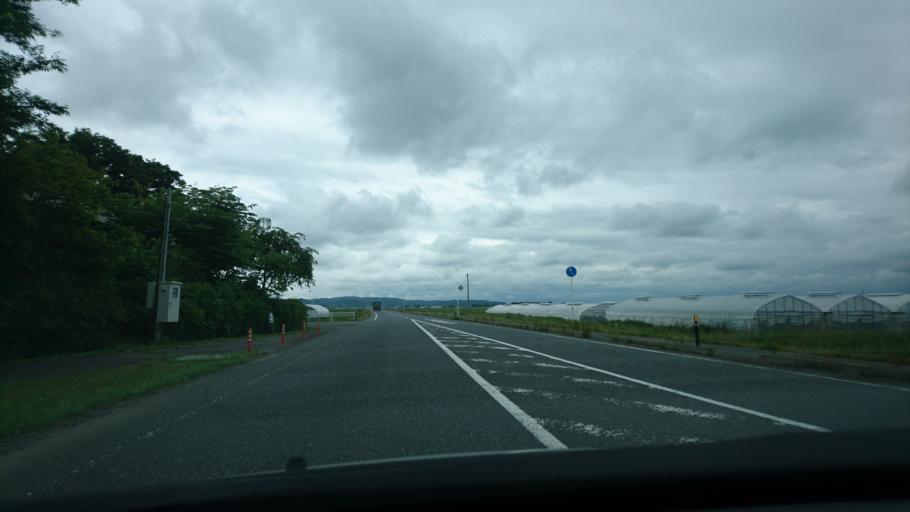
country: JP
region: Miyagi
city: Wakuya
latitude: 38.6951
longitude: 141.2604
